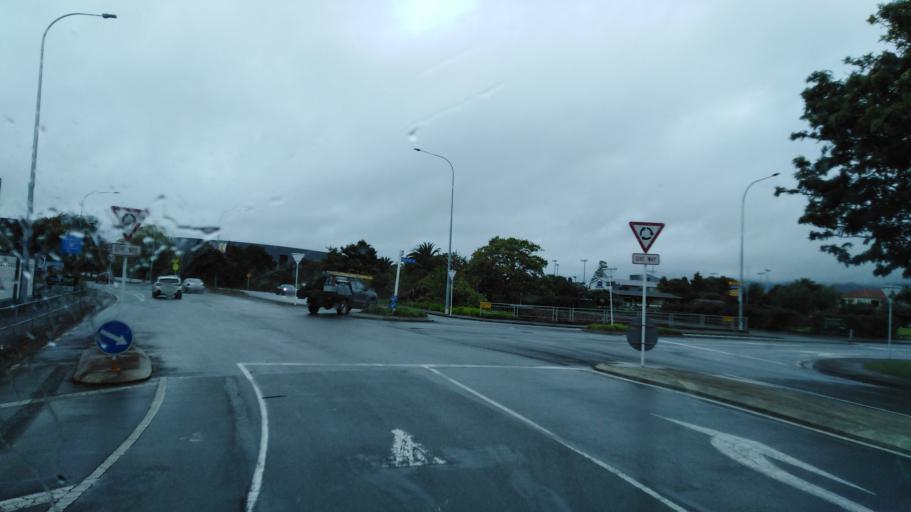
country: NZ
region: Nelson
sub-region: Nelson City
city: Nelson
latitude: -41.2709
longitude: 173.2789
